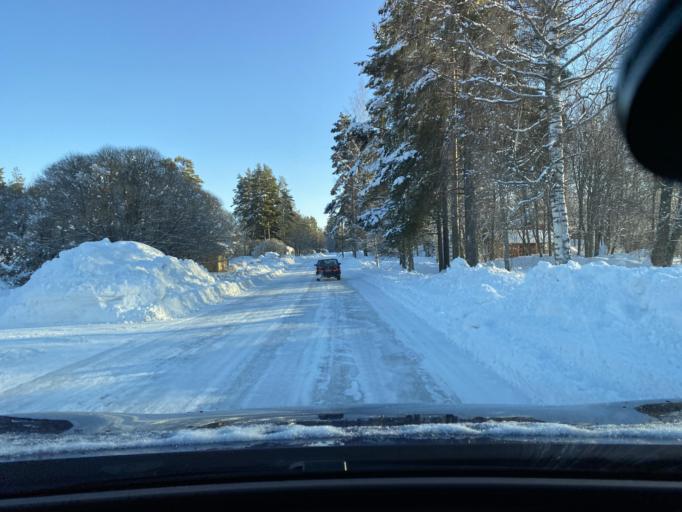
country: FI
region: Southern Savonia
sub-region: Mikkeli
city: Kangasniemi
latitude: 61.9989
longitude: 26.6284
